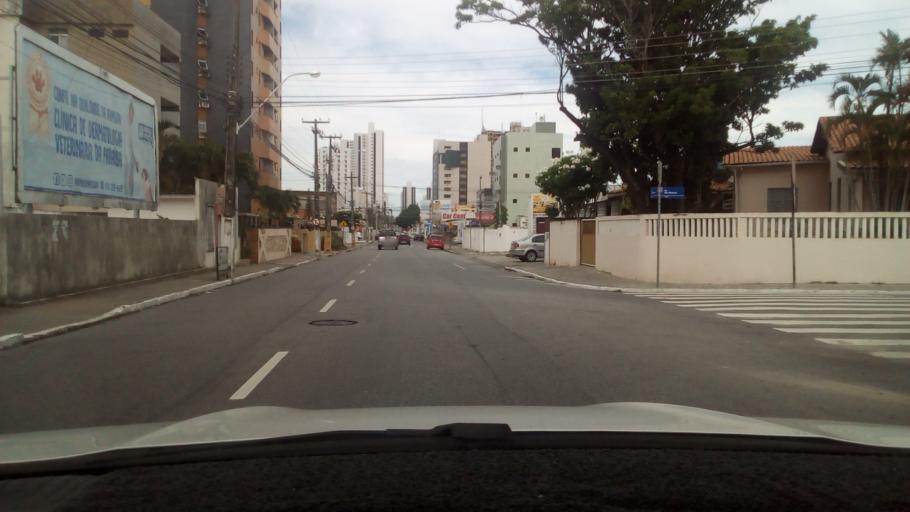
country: BR
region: Paraiba
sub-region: Joao Pessoa
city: Joao Pessoa
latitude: -7.1212
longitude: -34.8582
